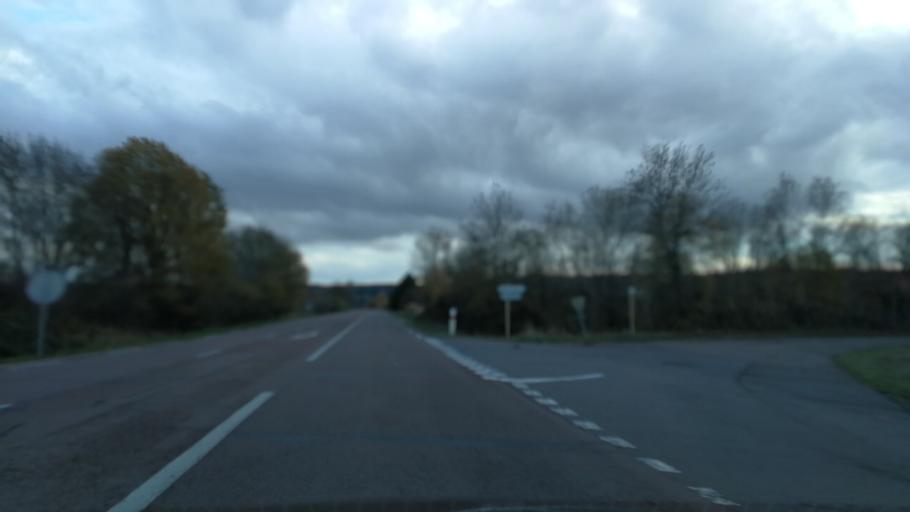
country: FR
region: Bourgogne
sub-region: Departement de la Cote-d'Or
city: Saulieu
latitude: 47.2671
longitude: 4.2578
